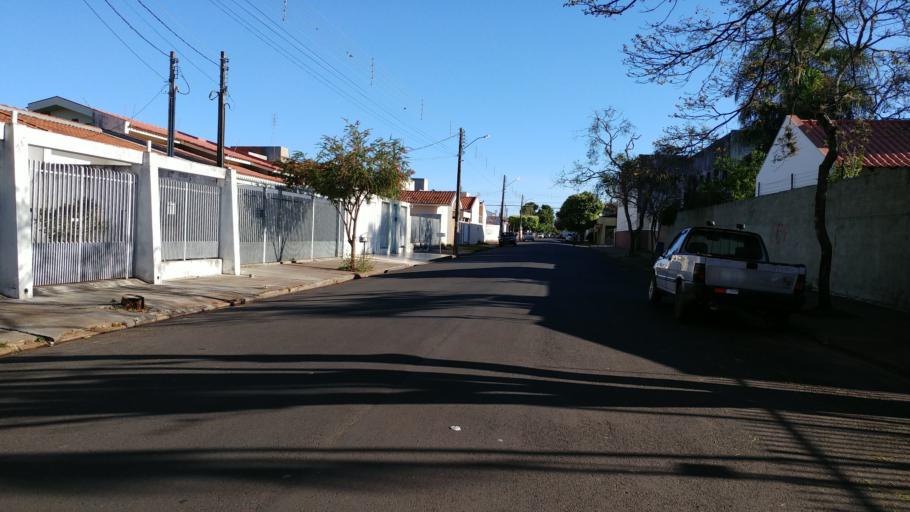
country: BR
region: Sao Paulo
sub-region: Paraguacu Paulista
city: Paraguacu Paulista
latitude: -22.4238
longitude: -50.5811
